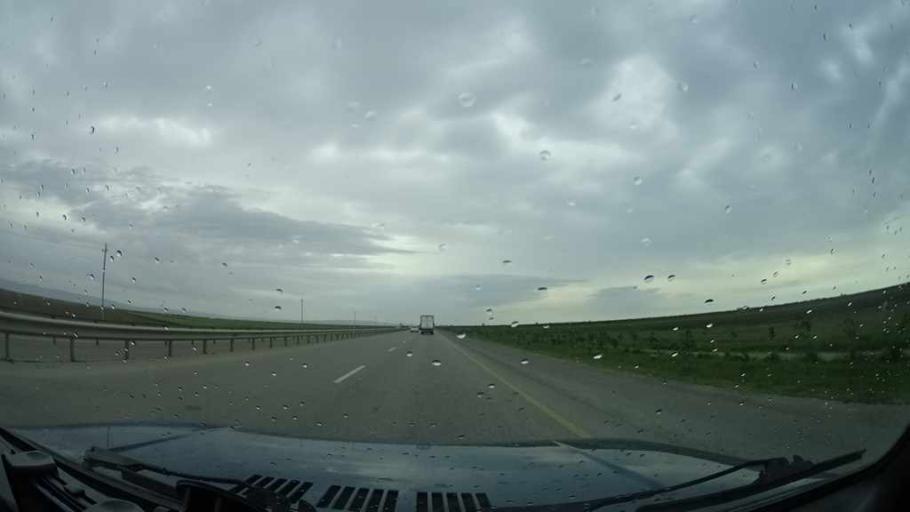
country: AZ
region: Goranboy
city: Goranboy
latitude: 40.6444
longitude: 46.7174
